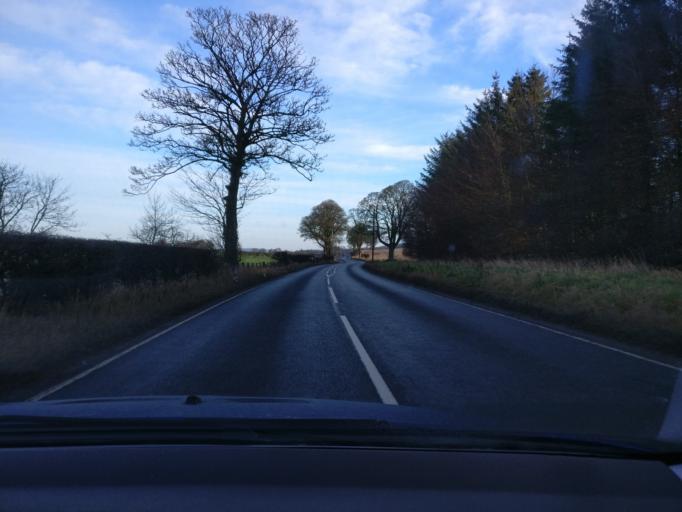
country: GB
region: Scotland
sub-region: The Scottish Borders
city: Saint Boswells
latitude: 55.4643
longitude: -2.6682
